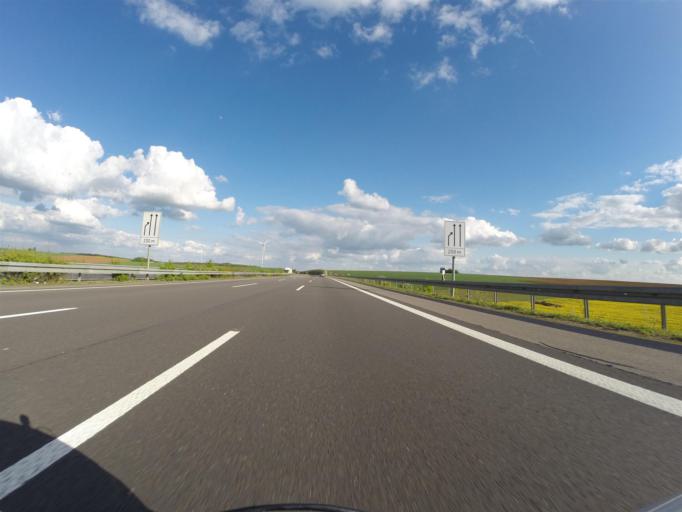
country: DE
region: Saarland
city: Perl
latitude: 49.4731
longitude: 6.4355
